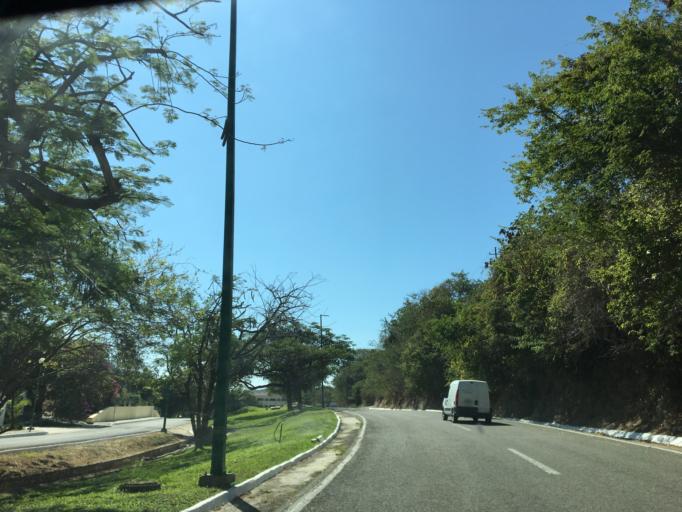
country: MX
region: Oaxaca
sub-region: Santa Maria Huatulco
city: Crucecita
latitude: 15.7775
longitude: -96.0919
